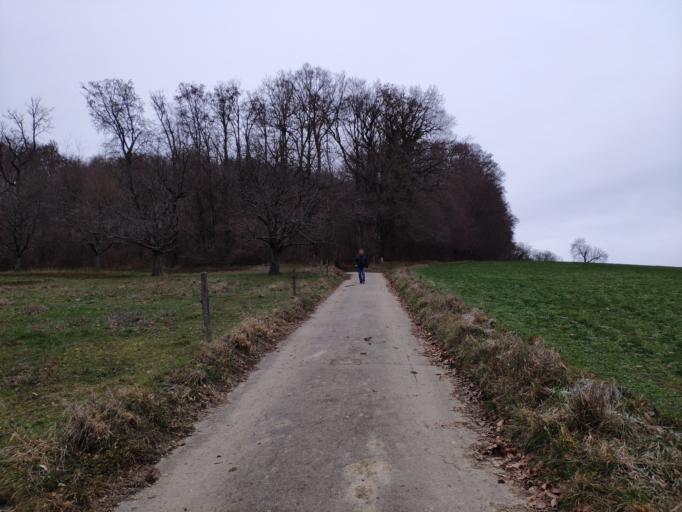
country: DE
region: Baden-Wuerttemberg
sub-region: Freiburg Region
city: Inzlingen
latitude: 47.5910
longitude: 7.6769
